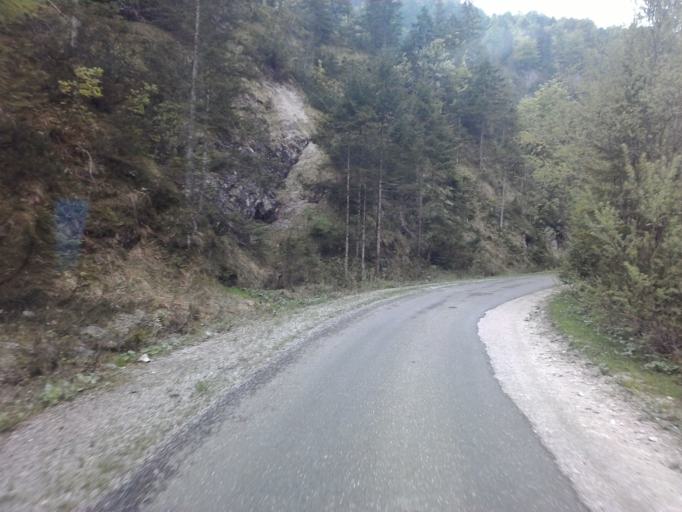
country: AT
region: Styria
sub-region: Politischer Bezirk Liezen
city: Wildalpen
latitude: 47.7014
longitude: 14.9985
